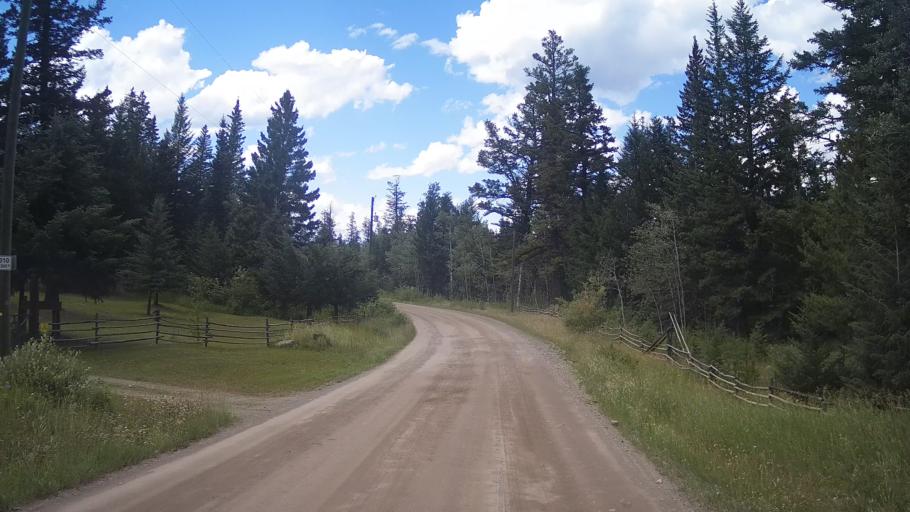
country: CA
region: British Columbia
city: Lillooet
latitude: 51.3081
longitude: -121.8199
